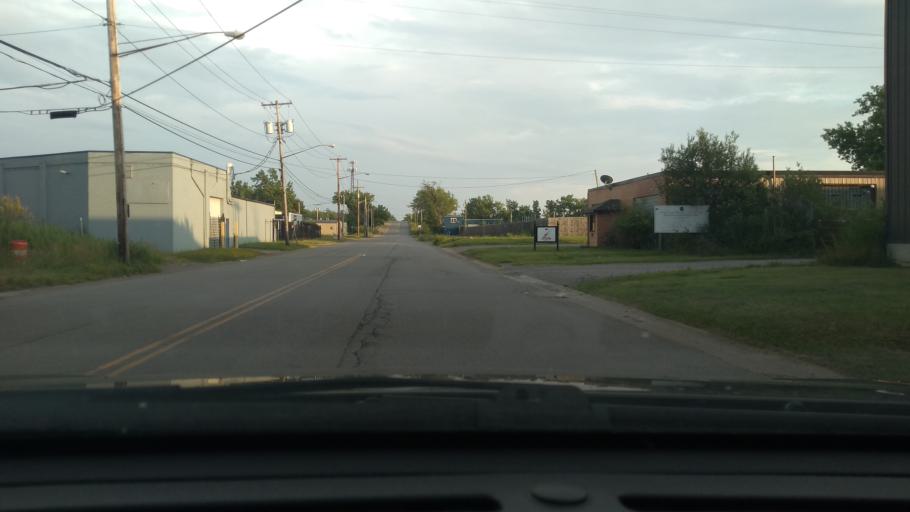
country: US
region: New York
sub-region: Erie County
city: Lackawanna
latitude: 42.8405
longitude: -78.8325
